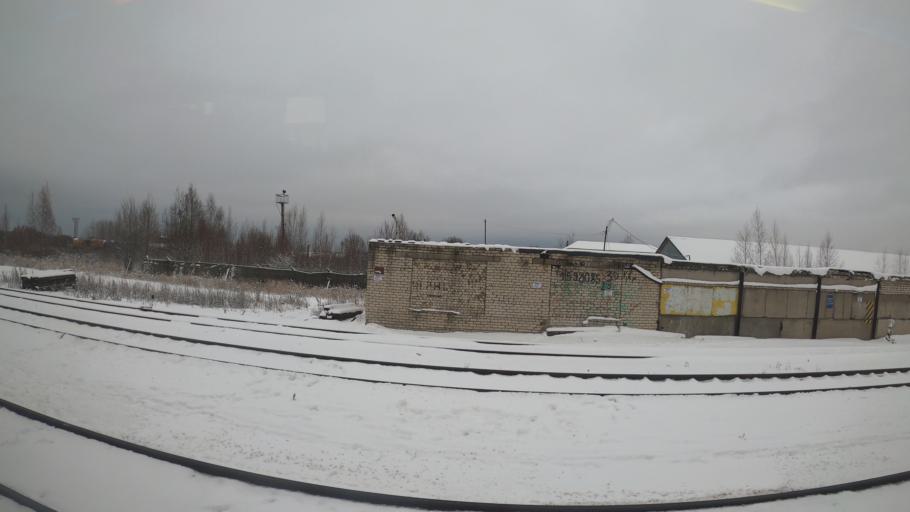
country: RU
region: Jaroslavl
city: Pereslavl'-Zalesskiy
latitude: 56.7351
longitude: 38.8859
